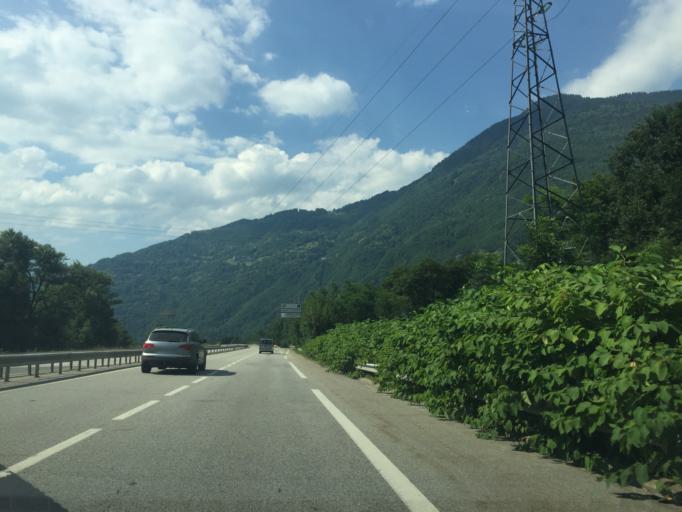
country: FR
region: Rhone-Alpes
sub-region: Departement de la Savoie
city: La Bathie
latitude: 45.6484
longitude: 6.4375
